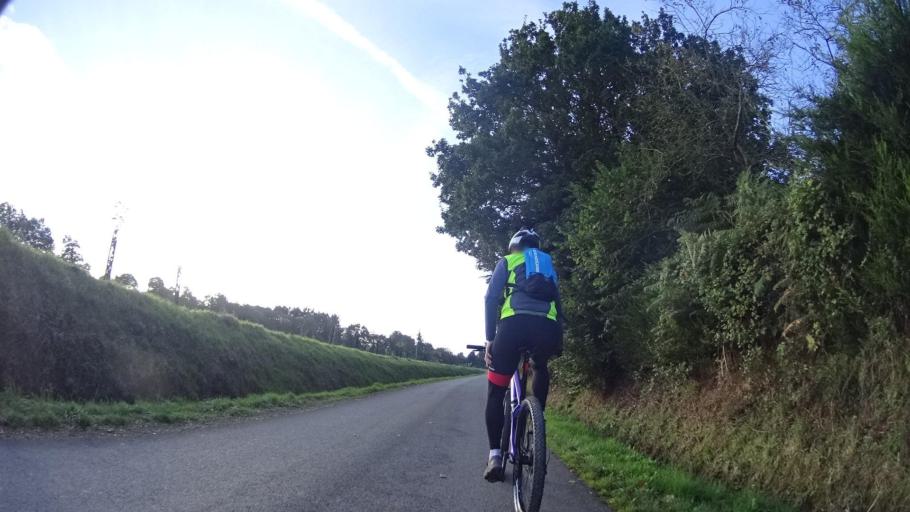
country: FR
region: Brittany
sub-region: Departement des Cotes-d'Armor
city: Evran
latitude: 48.3459
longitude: -1.9400
